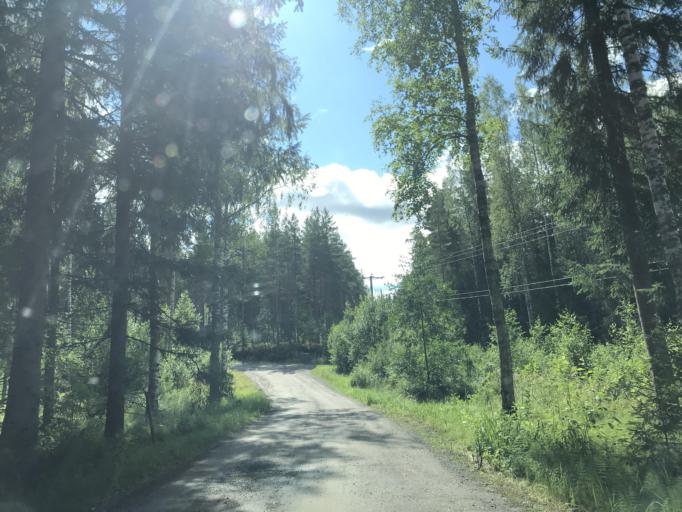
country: FI
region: Haeme
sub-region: Forssa
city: Tammela
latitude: 60.6278
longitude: 23.7580
